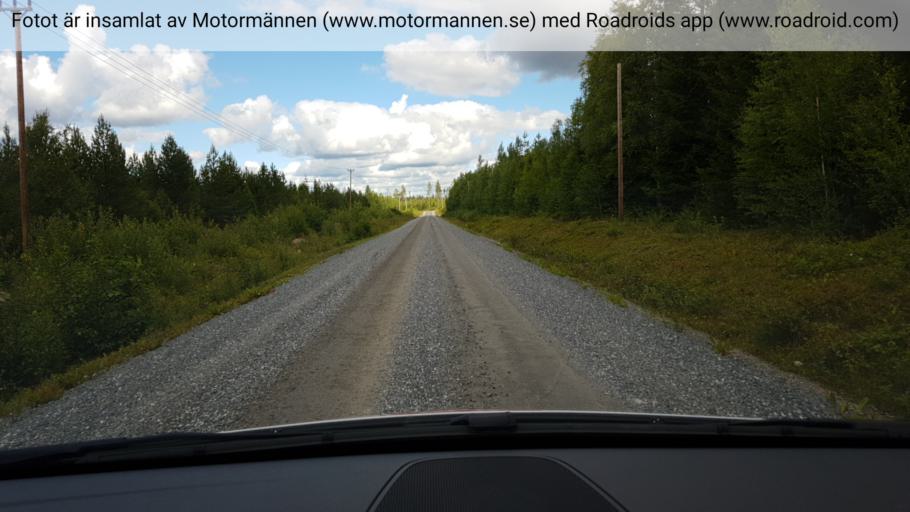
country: SE
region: Jaemtland
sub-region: Braecke Kommun
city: Braecke
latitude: 63.0552
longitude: 15.7280
